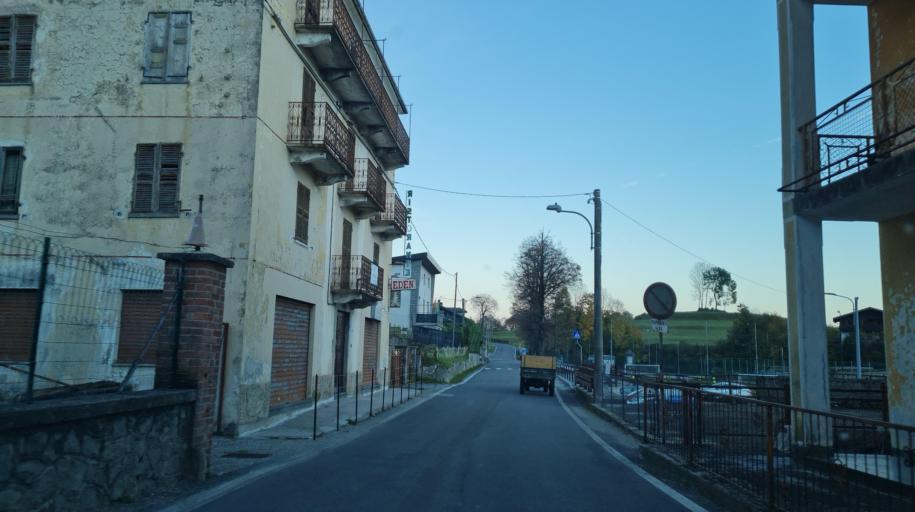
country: IT
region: Piedmont
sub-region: Provincia di Torino
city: Trausella
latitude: 45.4972
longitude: 7.7680
